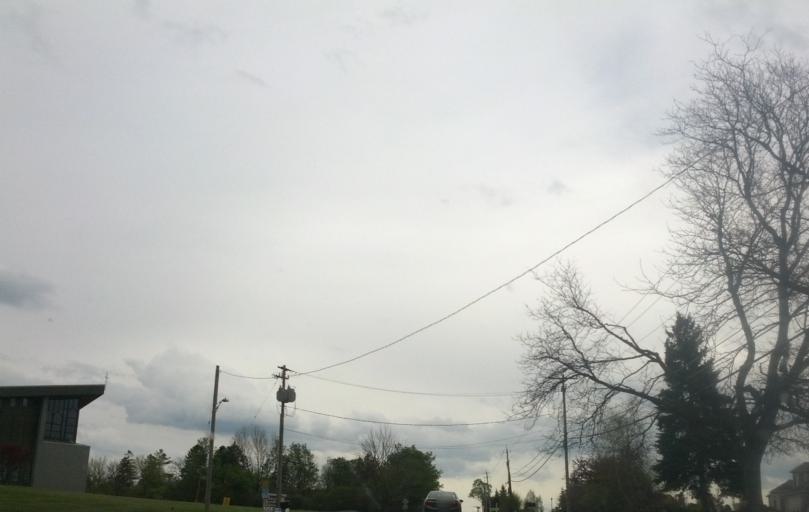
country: US
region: New York
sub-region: Onondaga County
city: Nedrow
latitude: 42.9978
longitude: -76.1177
